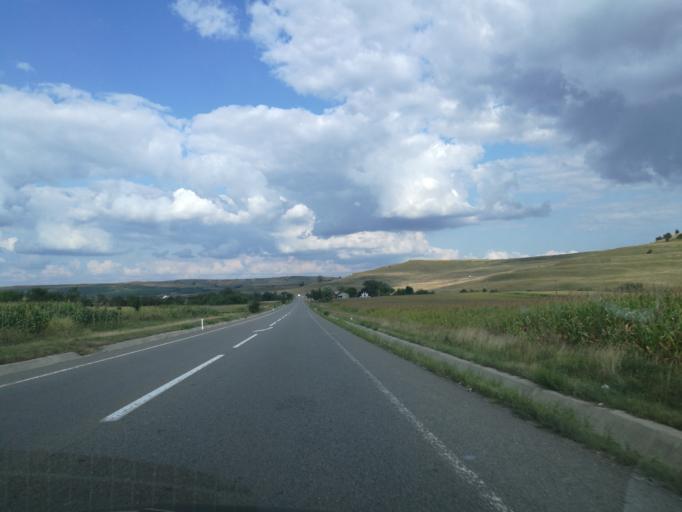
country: RO
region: Suceava
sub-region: Comuna Ilisesti
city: Ilisesti
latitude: 47.6137
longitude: 26.0666
